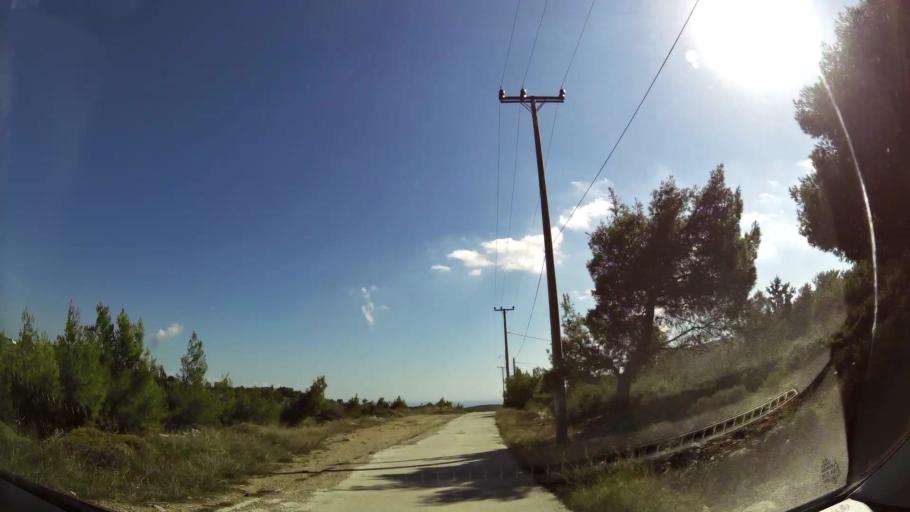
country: GR
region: Attica
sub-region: Nomarchia Anatolikis Attikis
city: Dioni
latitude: 38.0366
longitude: 23.9405
